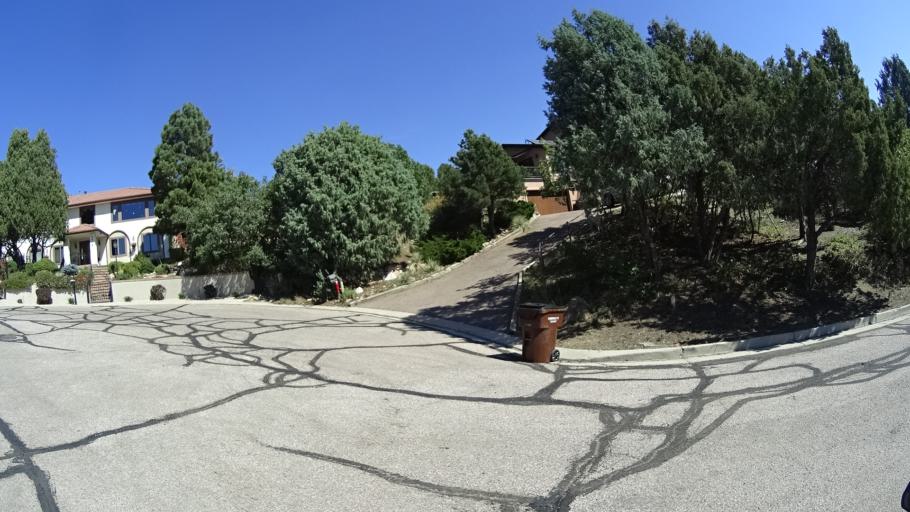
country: US
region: Colorado
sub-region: El Paso County
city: Cimarron Hills
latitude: 38.9151
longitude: -104.7527
